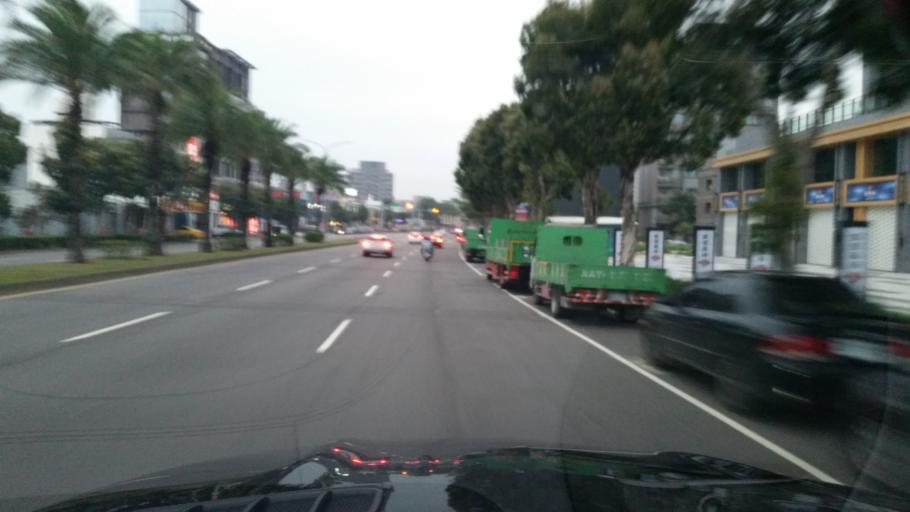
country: TW
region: Taiwan
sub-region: Taoyuan
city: Taoyuan
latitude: 25.0675
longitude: 121.3559
